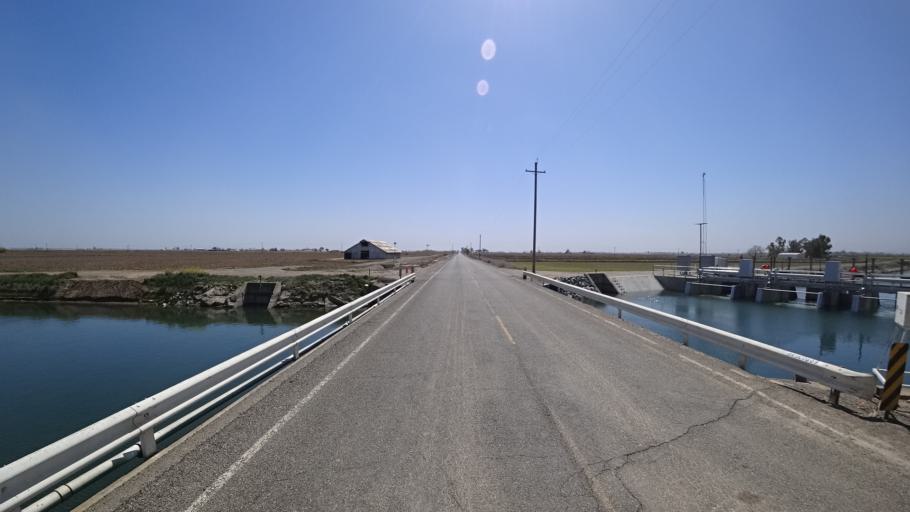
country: US
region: California
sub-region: Glenn County
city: Willows
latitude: 39.5568
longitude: -122.1370
